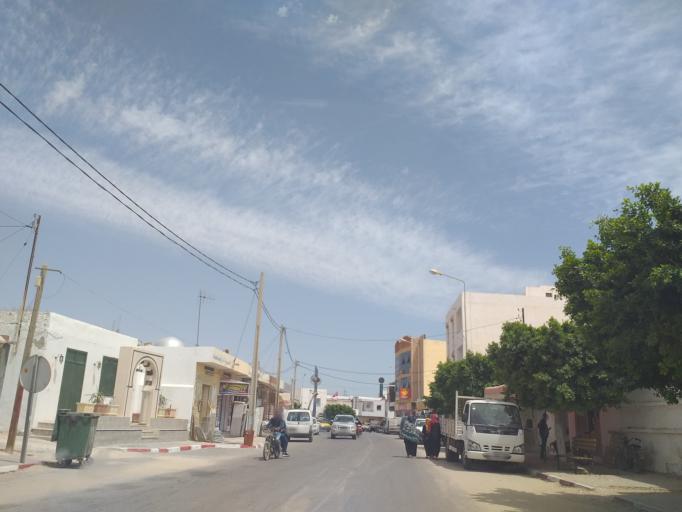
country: TN
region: Qabis
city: Gabes
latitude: 33.9389
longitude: 10.0651
